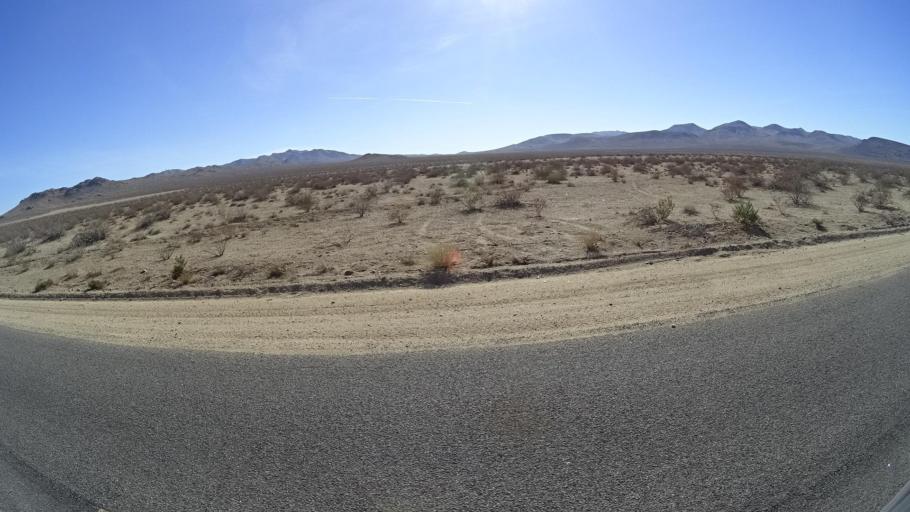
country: US
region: California
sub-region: Kern County
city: Ridgecrest
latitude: 35.5510
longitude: -117.7212
